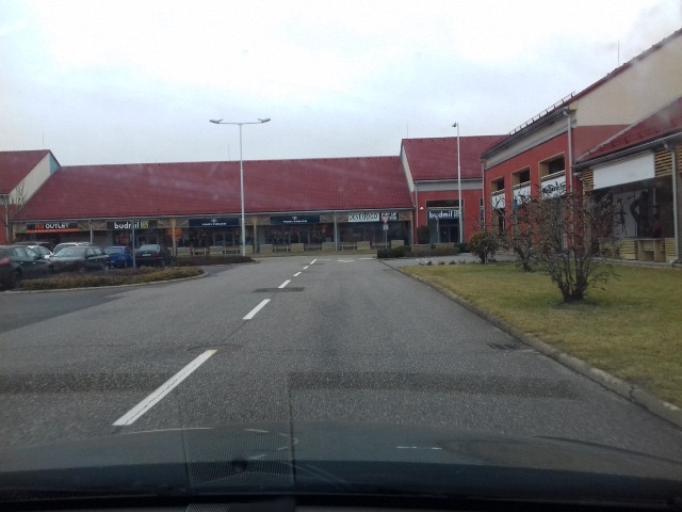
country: HU
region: Hajdu-Bihar
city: Polgar
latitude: 47.8435
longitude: 21.1441
